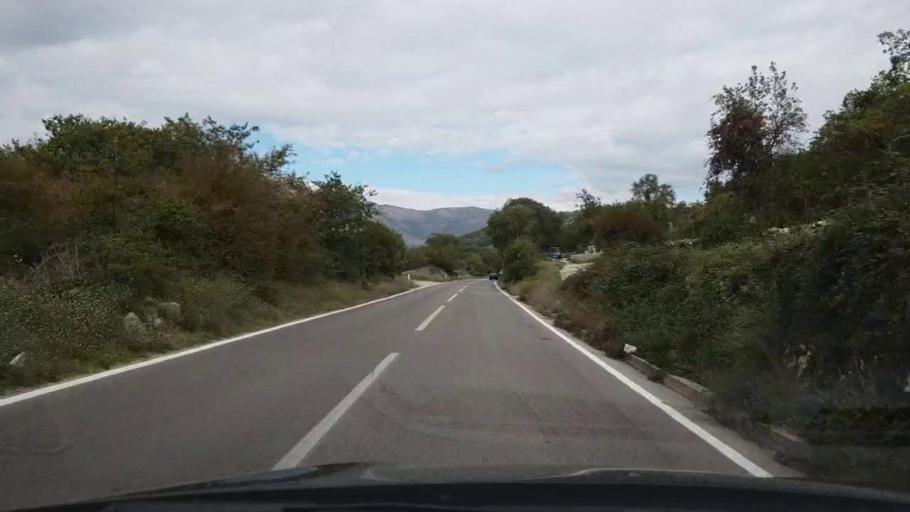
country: BA
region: Republika Srpska
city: Trebinje
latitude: 42.6831
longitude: 18.3035
